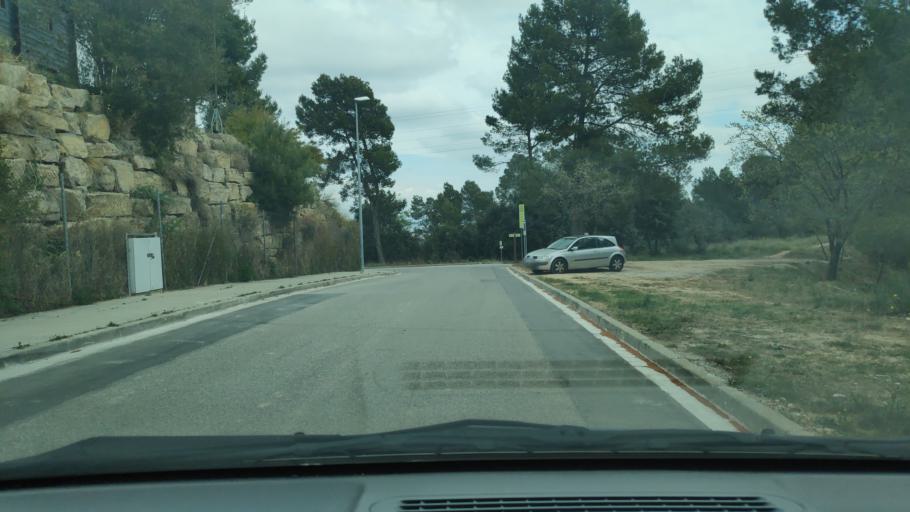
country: ES
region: Catalonia
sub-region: Provincia de Barcelona
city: Sant Quirze del Valles
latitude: 41.5126
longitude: 2.0642
